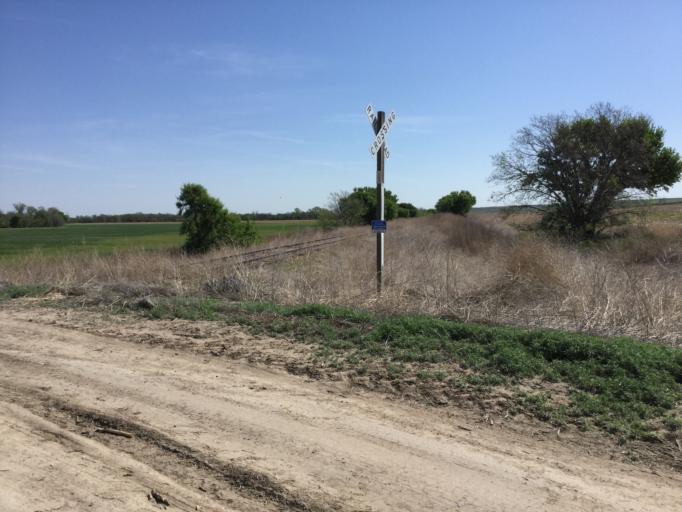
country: US
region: Kansas
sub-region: Decatur County
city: Oberlin
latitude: 39.9485
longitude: -100.6092
